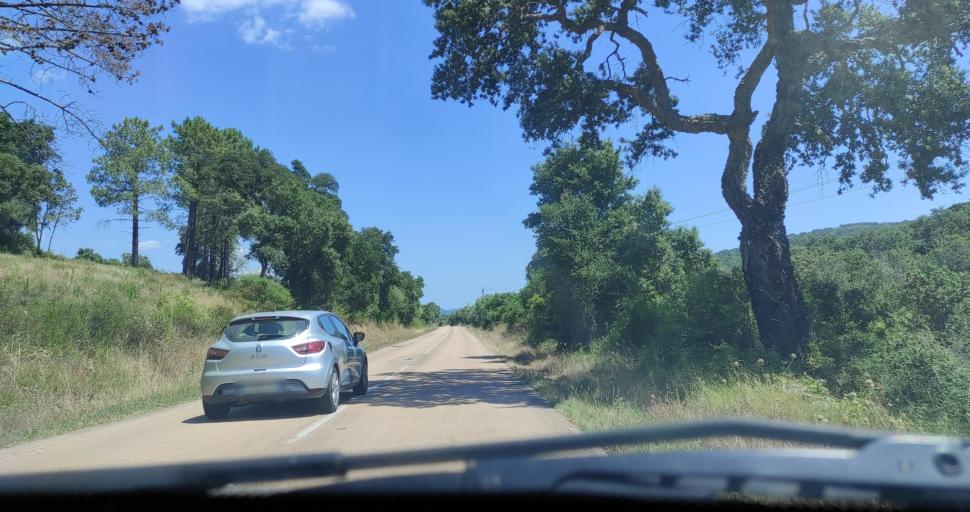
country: FR
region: Corsica
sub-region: Departement de la Corse-du-Sud
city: Porto-Vecchio
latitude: 41.5390
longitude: 9.1754
